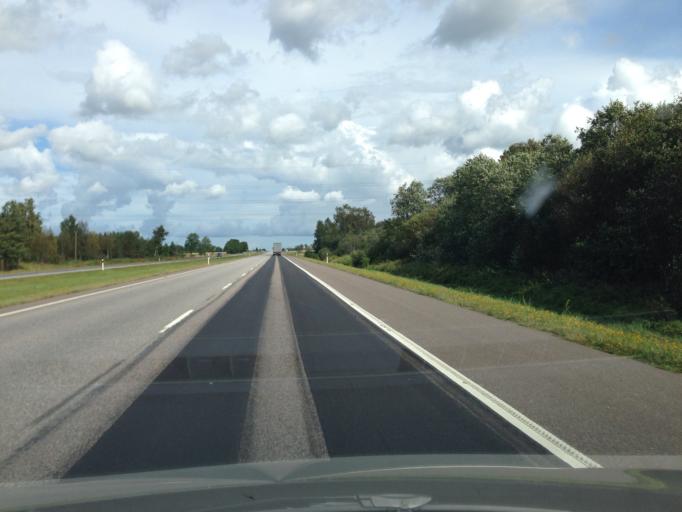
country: EE
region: Harju
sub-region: Saue linn
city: Saue
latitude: 59.2941
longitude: 24.5475
